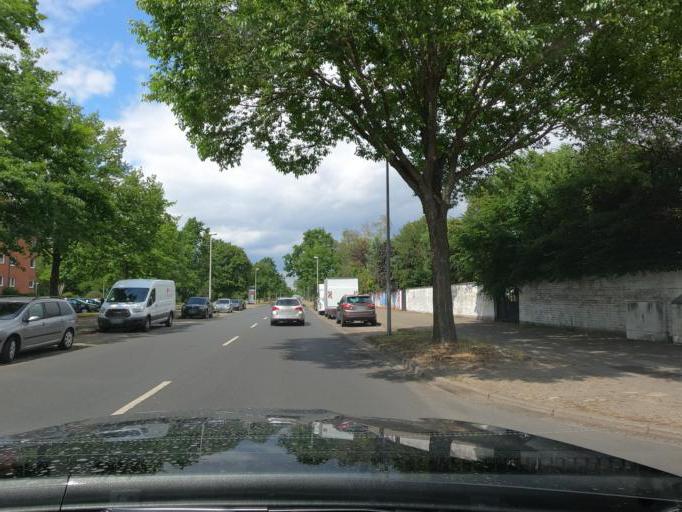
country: DE
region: Lower Saxony
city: Laatzen
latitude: 52.3935
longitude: 9.8174
